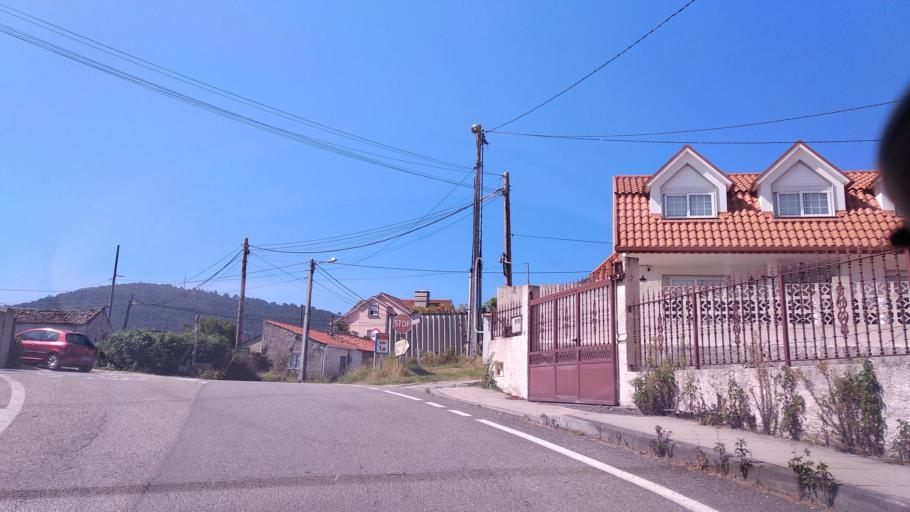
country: ES
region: Galicia
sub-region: Provincia de Pontevedra
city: Moana
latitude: 42.2778
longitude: -8.7687
